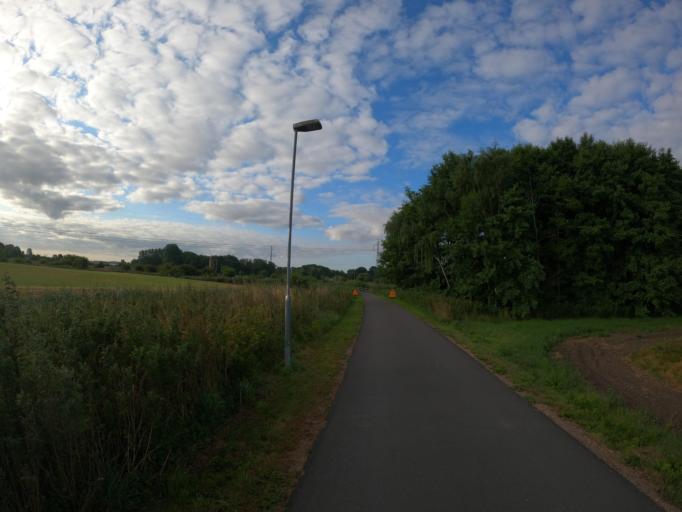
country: SE
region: Skane
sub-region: Staffanstorps Kommun
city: Staffanstorp
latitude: 55.6591
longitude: 13.2117
